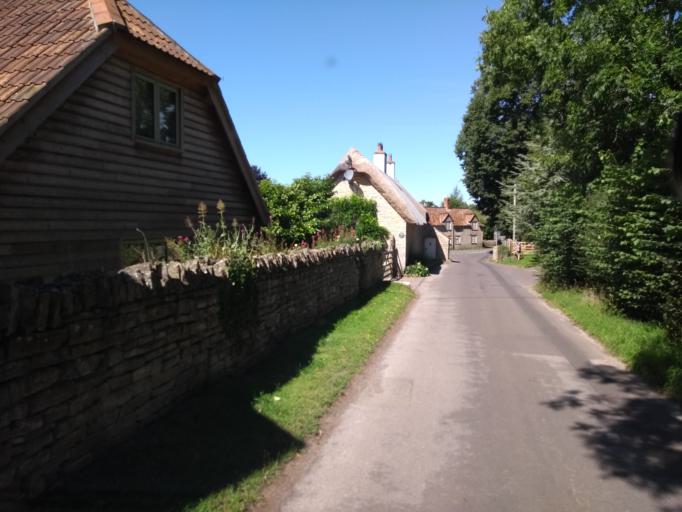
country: GB
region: England
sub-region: Somerset
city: Ilchester
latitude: 51.0580
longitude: -2.6709
